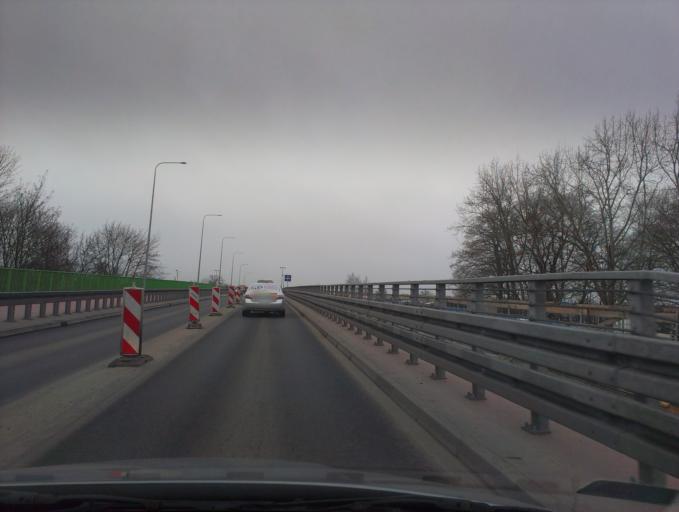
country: PL
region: Greater Poland Voivodeship
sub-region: Powiat pilski
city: Pila
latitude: 53.1446
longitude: 16.7397
